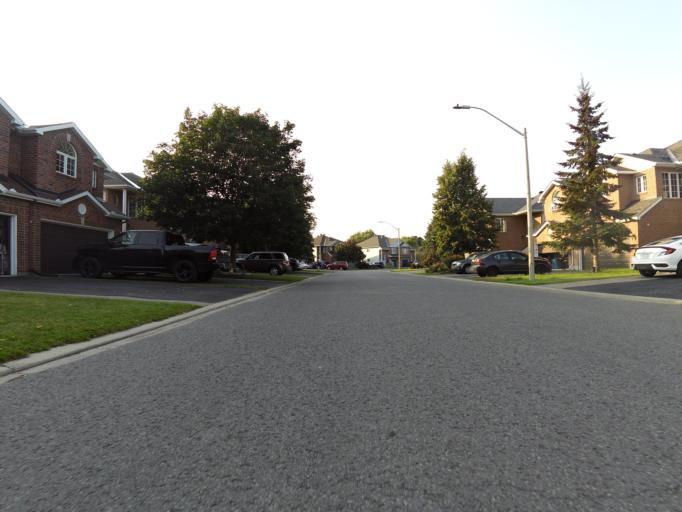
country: CA
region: Ontario
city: Bells Corners
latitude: 45.2844
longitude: -75.8841
